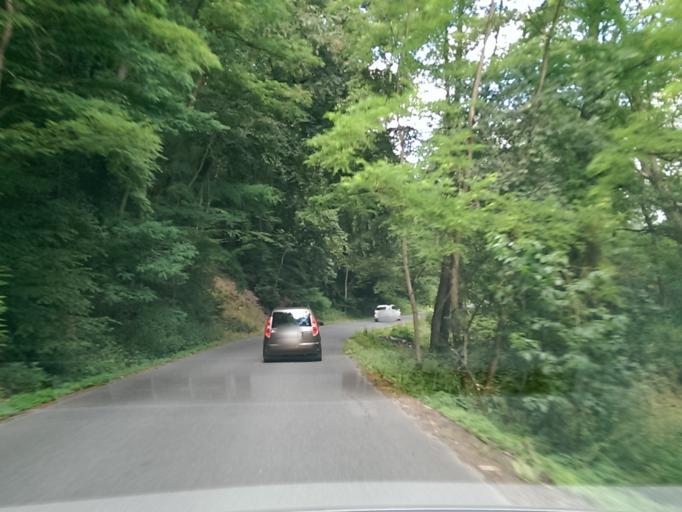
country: CZ
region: Central Bohemia
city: Mseno
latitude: 50.4250
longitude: 14.5748
